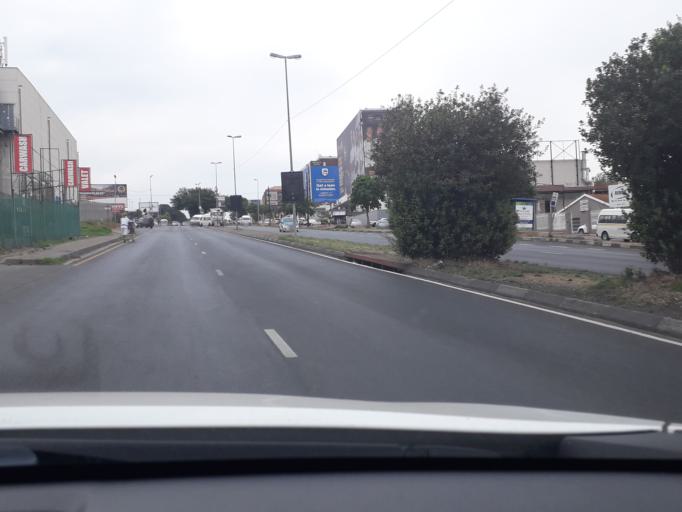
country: ZA
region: Gauteng
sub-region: City of Johannesburg Metropolitan Municipality
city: Johannesburg
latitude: -26.0977
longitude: 28.0095
